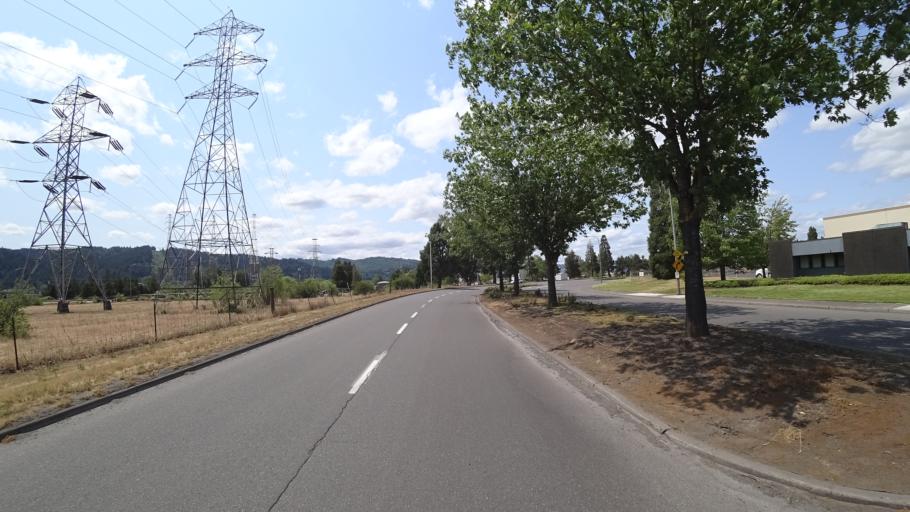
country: US
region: Oregon
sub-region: Washington County
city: Cedar Mill
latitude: 45.6186
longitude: -122.7789
